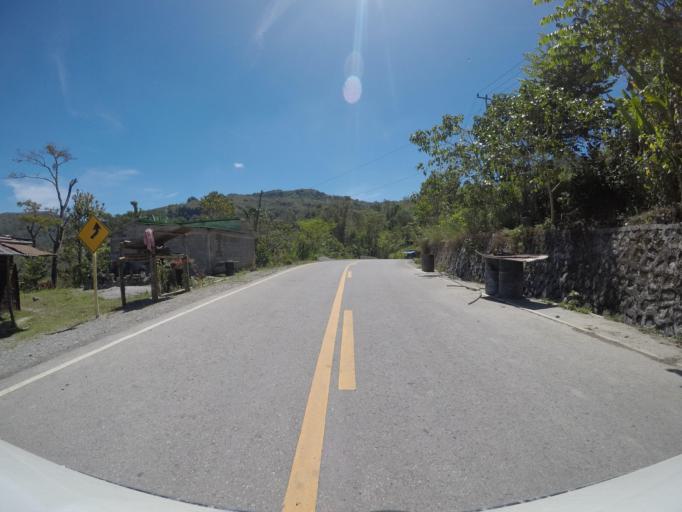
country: TL
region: Manatuto
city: Manatuto
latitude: -8.7797
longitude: 125.9677
